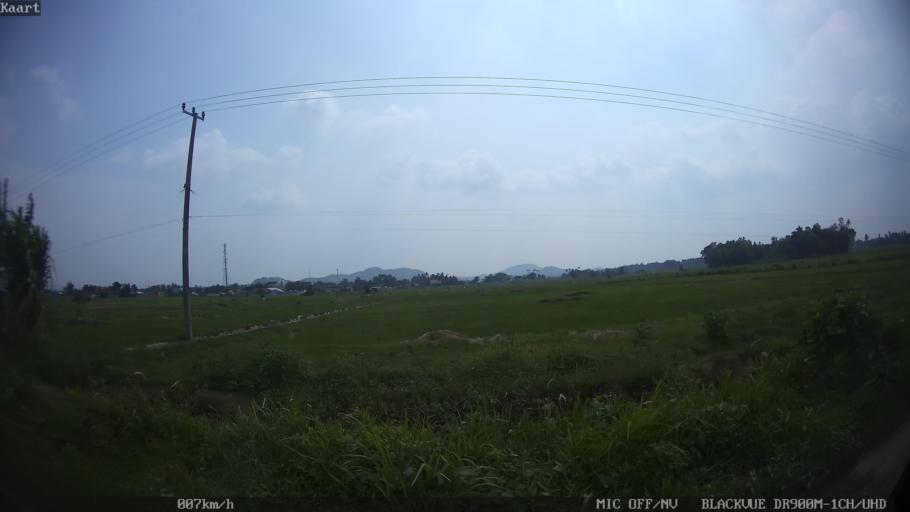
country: ID
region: Lampung
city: Gadingrejo
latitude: -5.3674
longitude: 105.0504
